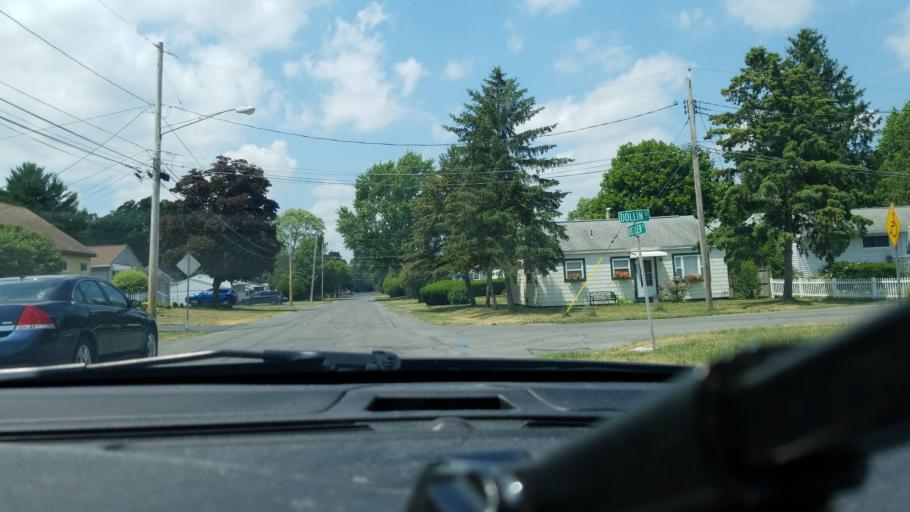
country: US
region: New York
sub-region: Onondaga County
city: Galeville
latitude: 43.0921
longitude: -76.1758
